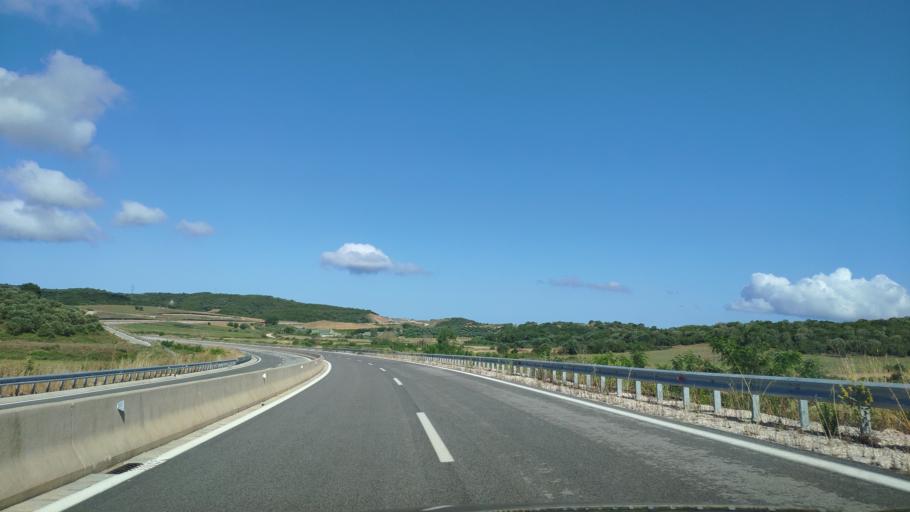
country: GR
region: West Greece
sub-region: Nomos Aitolias kai Akarnanias
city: Vonitsa
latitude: 38.9114
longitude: 20.8434
